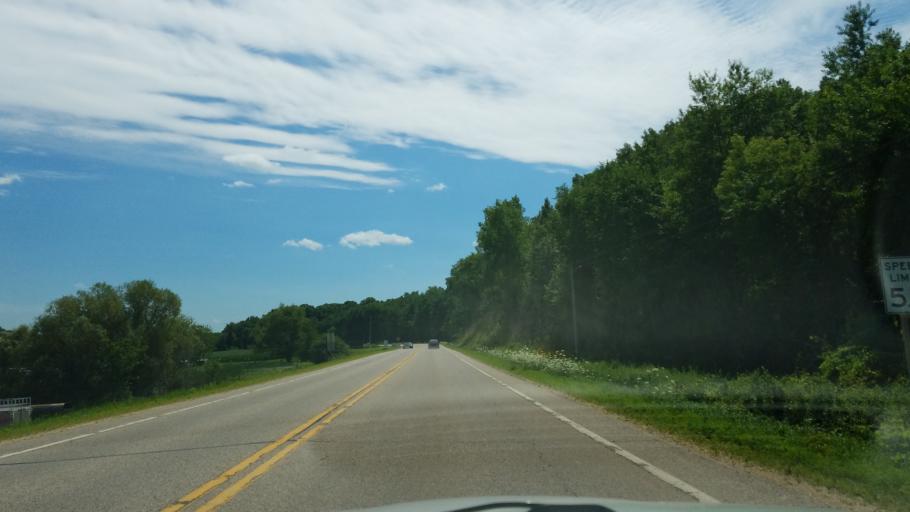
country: US
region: Wisconsin
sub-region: Saint Croix County
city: Glenwood City
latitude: 45.0538
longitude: -92.1774
